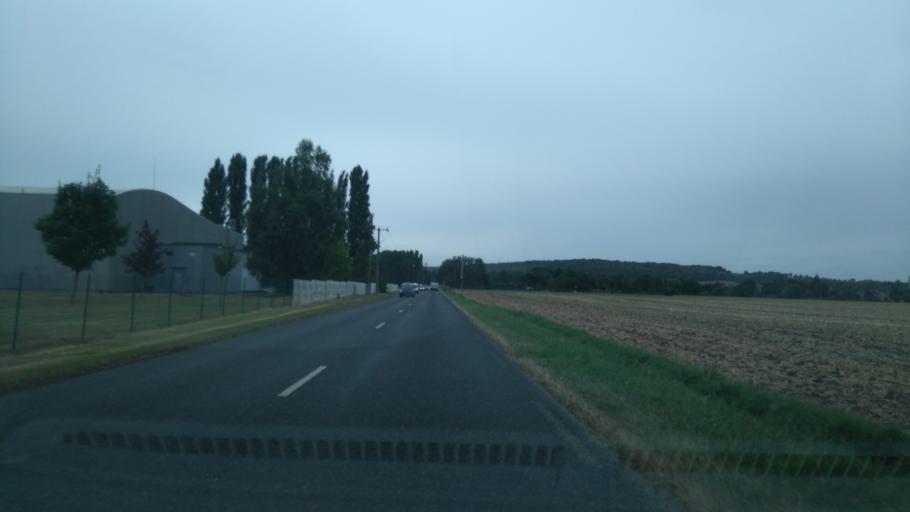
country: FR
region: Picardie
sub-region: Departement de l'Oise
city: Precy-sur-Oise
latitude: 49.1967
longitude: 2.3801
